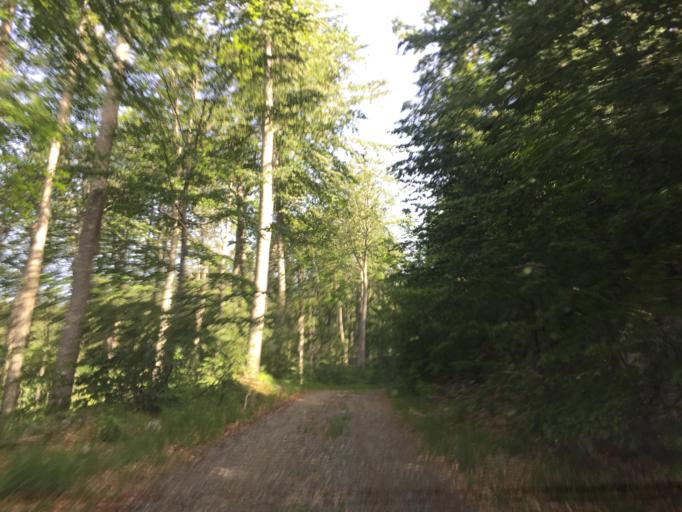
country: HR
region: Primorsko-Goranska
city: Podhum
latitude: 45.4195
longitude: 14.5876
